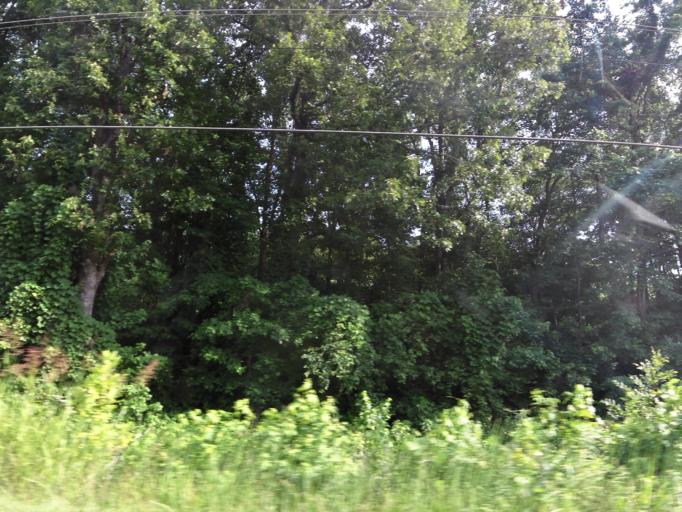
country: US
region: Tennessee
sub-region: Benton County
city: Camden
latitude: 36.0455
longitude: -88.1585
